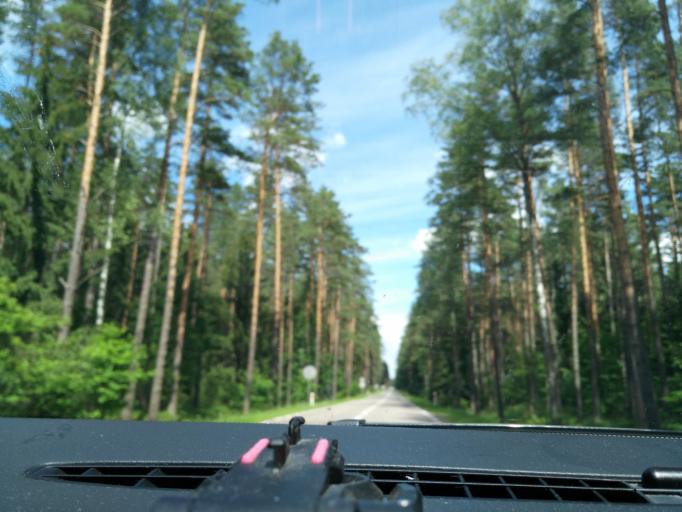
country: PL
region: Podlasie
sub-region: Powiat sejnenski
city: Krasnopol
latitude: 53.9652
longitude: 23.2401
